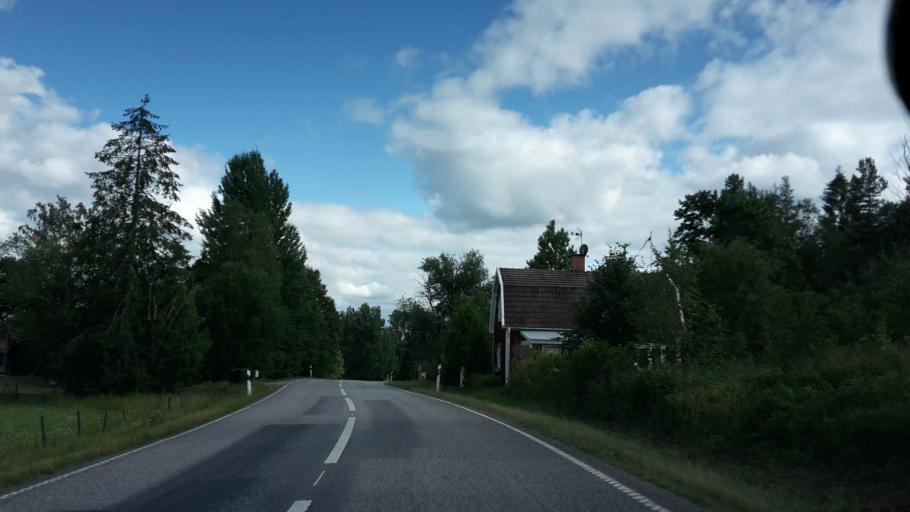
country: SE
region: OEstergoetland
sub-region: Linkopings Kommun
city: Ljungsbro
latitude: 58.7947
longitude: 15.4624
